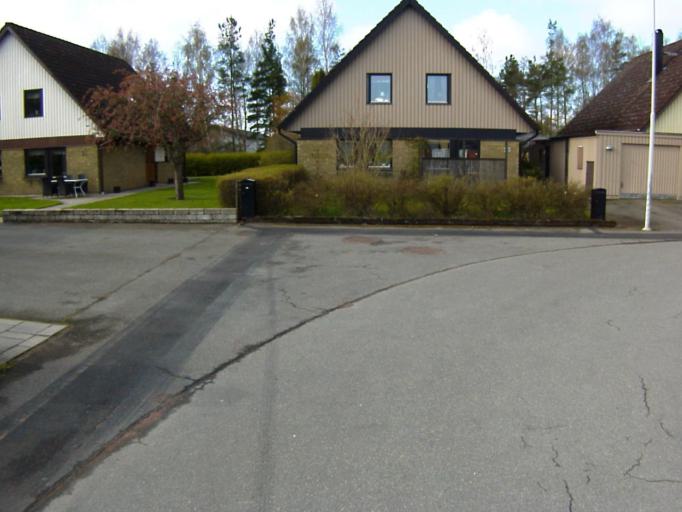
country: SE
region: Skane
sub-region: Kristianstads Kommun
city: Norra Asum
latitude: 56.0093
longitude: 14.1075
